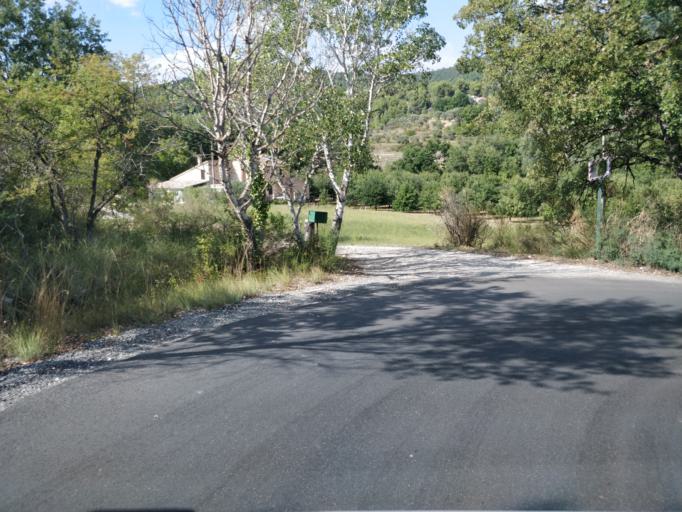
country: FR
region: Provence-Alpes-Cote d'Azur
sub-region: Departement des Alpes-de-Haute-Provence
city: Riez
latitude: 43.8413
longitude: 6.2078
